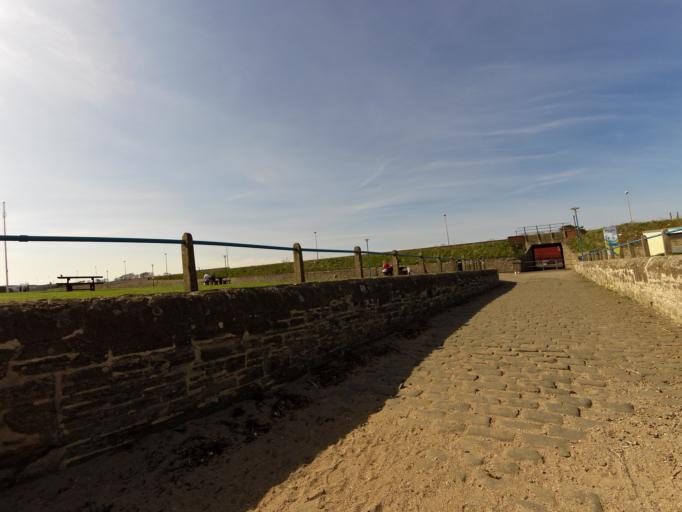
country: GB
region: Scotland
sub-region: Angus
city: Arbroath
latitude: 56.5518
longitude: -2.6006
